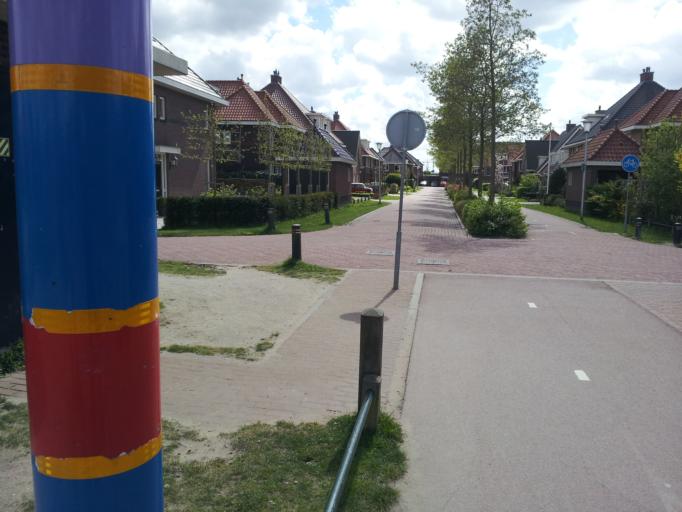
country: NL
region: South Holland
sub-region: Gemeente Lansingerland
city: Berkel en Rodenrijs
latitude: 51.9887
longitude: 4.4584
